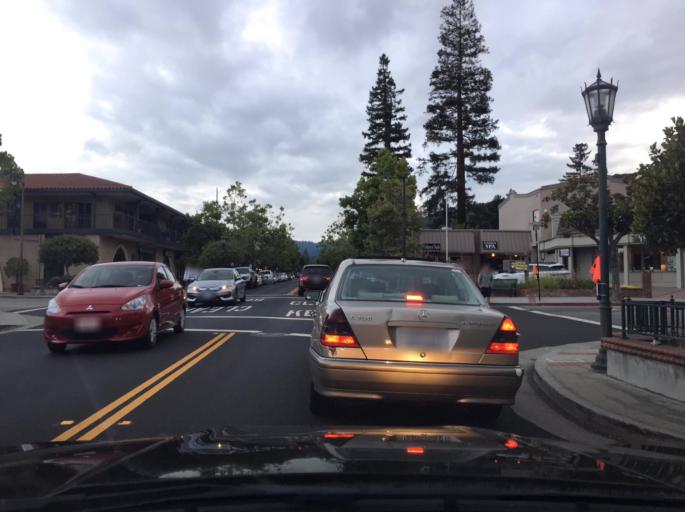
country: US
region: California
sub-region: Santa Clara County
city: Los Gatos
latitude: 37.2274
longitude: -121.9817
